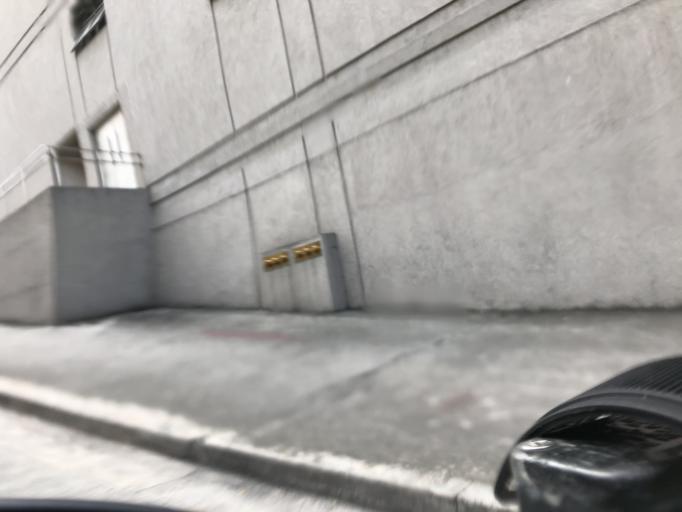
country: PH
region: Calabarzon
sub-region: Province of Rizal
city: San Mateo
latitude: 14.7372
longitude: 121.0603
